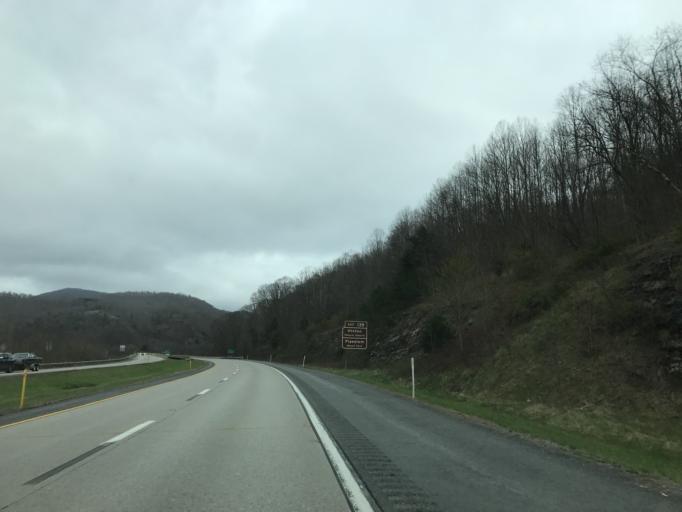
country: US
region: West Virginia
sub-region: Summers County
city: Hinton
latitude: 37.7818
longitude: -80.9062
